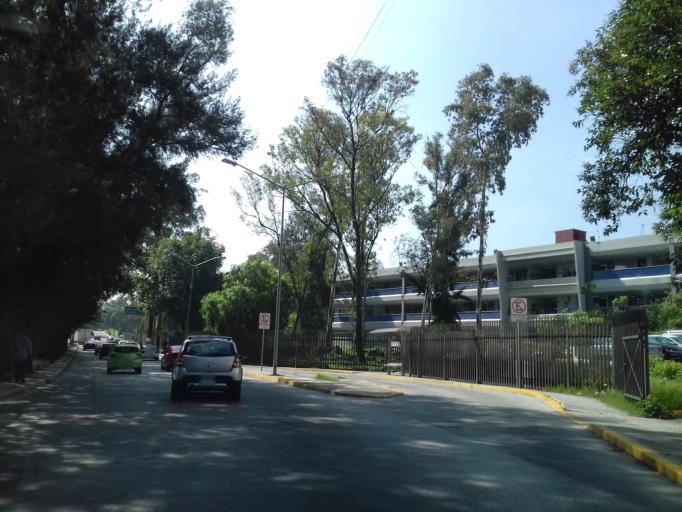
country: MX
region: Mexico City
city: Magdalena Contreras
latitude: 19.3329
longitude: -99.1964
